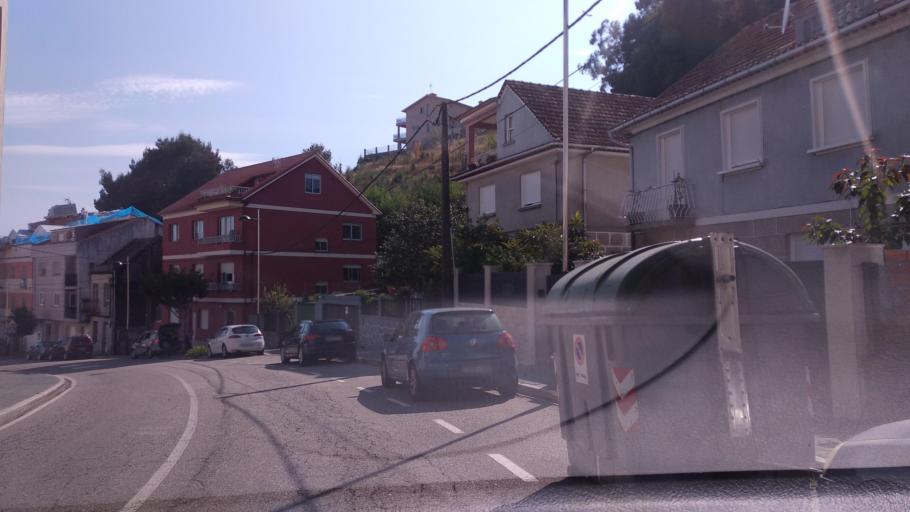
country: ES
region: Galicia
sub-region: Provincia de Pontevedra
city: Moana
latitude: 42.2738
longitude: -8.7422
